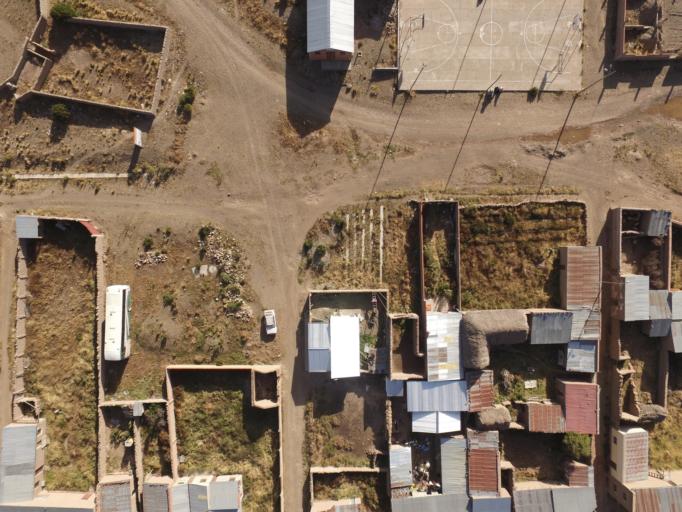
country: BO
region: Oruro
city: Challapata
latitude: -18.6916
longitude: -66.7578
